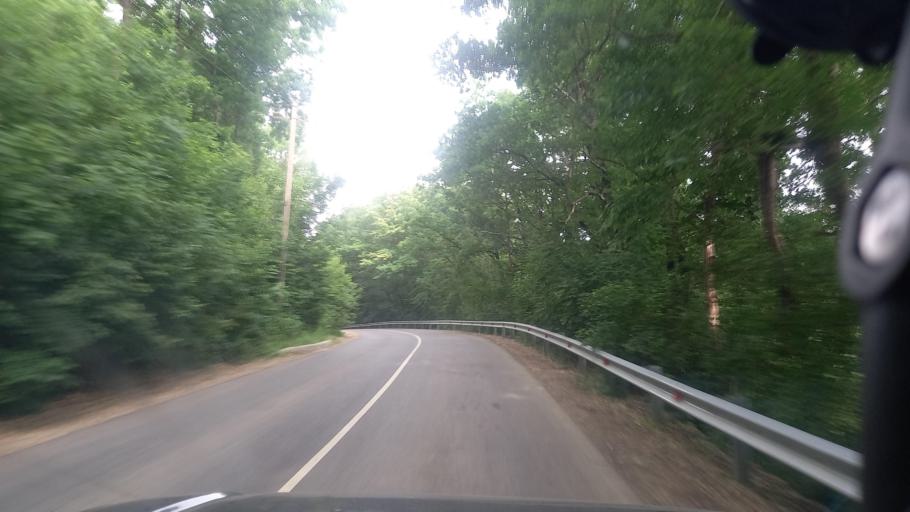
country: RU
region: Krasnodarskiy
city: Goryachiy Klyuch
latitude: 44.6042
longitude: 39.0037
